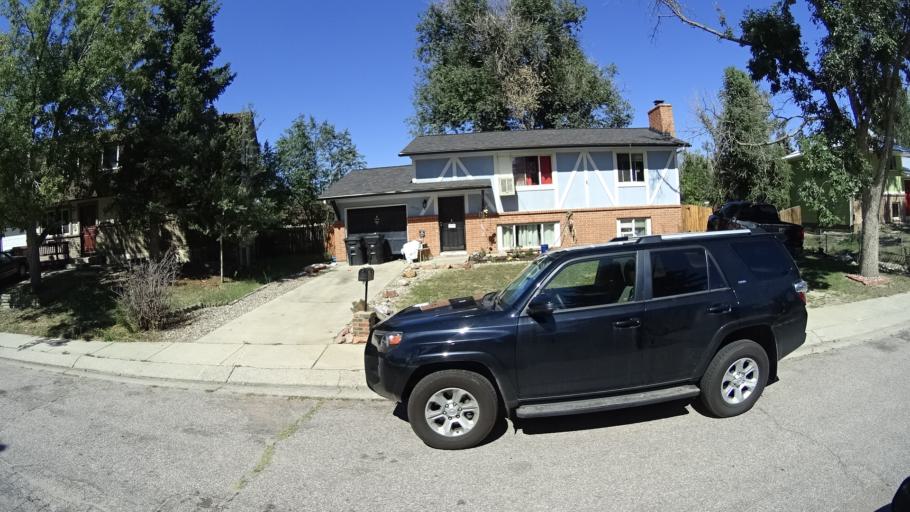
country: US
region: Colorado
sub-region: El Paso County
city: Cimarron Hills
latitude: 38.8788
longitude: -104.7372
